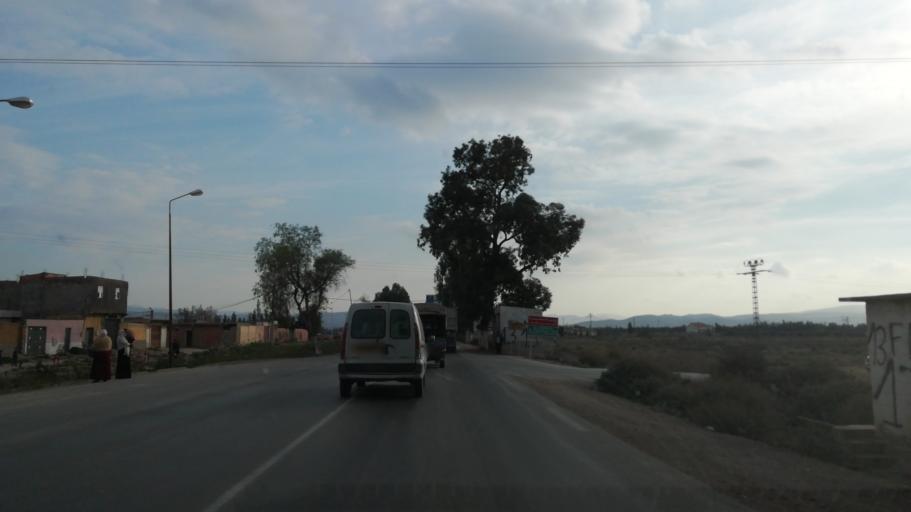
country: DZ
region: Mascara
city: Mascara
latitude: 35.6317
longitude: 0.0611
